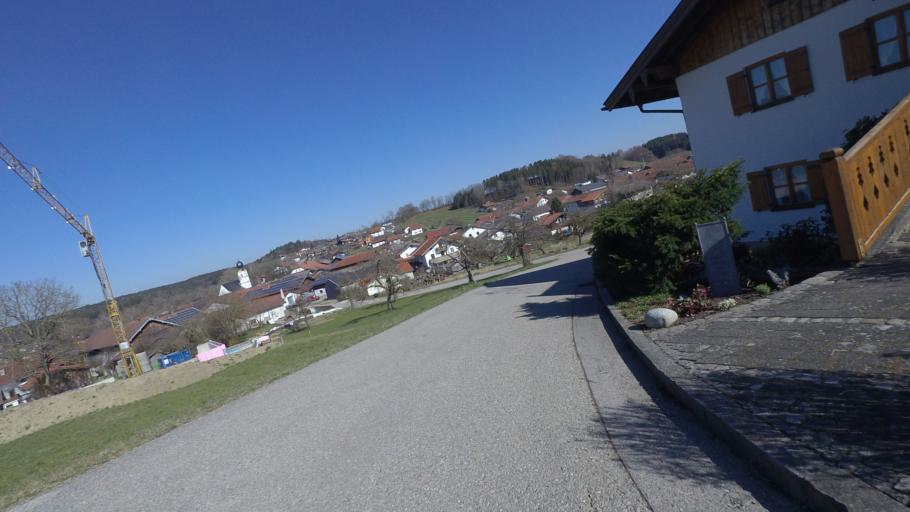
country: DE
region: Bavaria
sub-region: Upper Bavaria
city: Seeon-Seebruck
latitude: 47.9584
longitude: 12.4966
